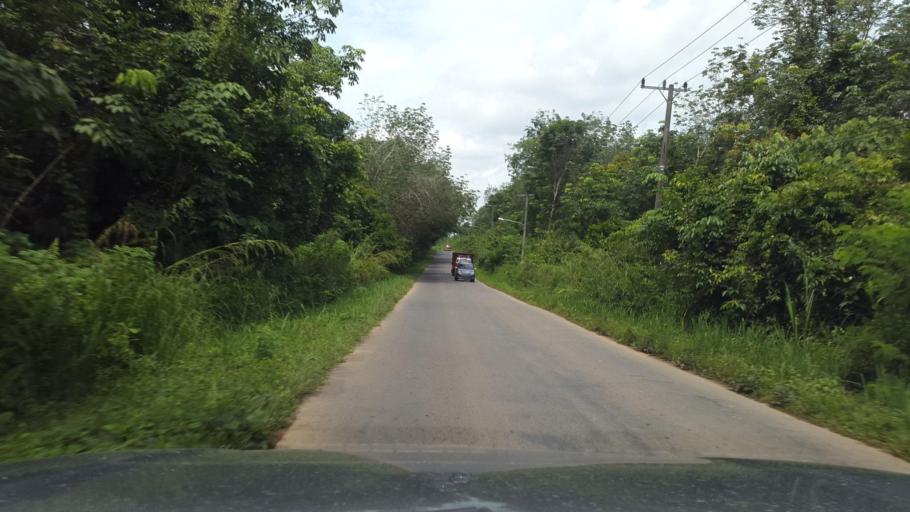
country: ID
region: South Sumatra
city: Gunungmegang Dalam
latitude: -3.3602
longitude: 103.9337
